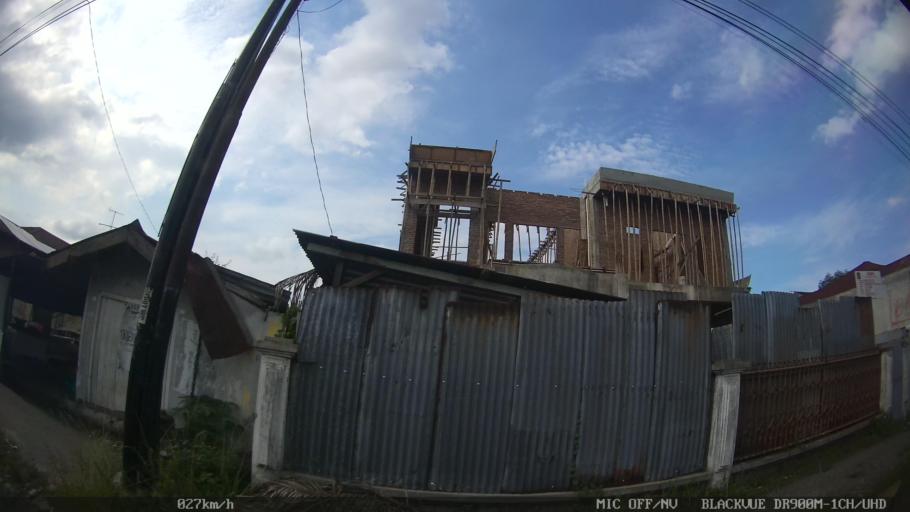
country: ID
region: North Sumatra
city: Medan
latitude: 3.6154
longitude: 98.6529
